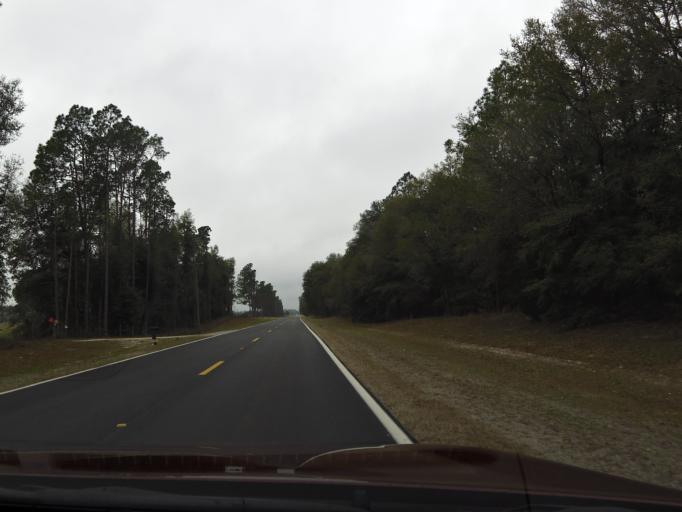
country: US
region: Florida
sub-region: Gilchrist County
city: Trenton
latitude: 29.7958
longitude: -82.8901
